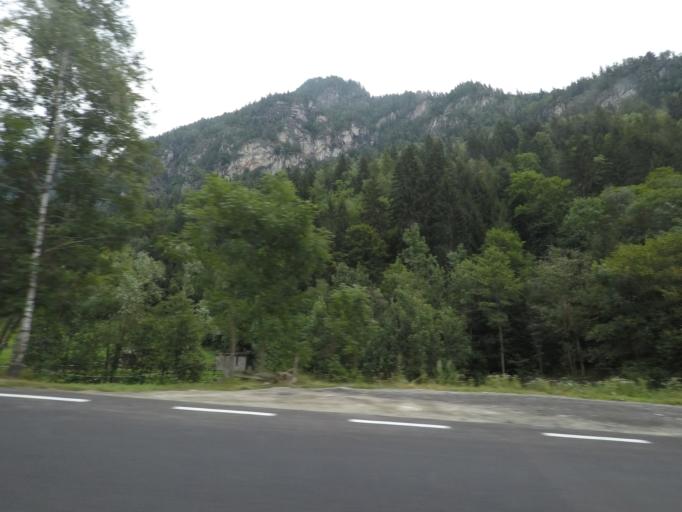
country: IT
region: Aosta Valley
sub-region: Valle d'Aosta
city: Chamois
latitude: 45.8287
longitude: 7.5989
